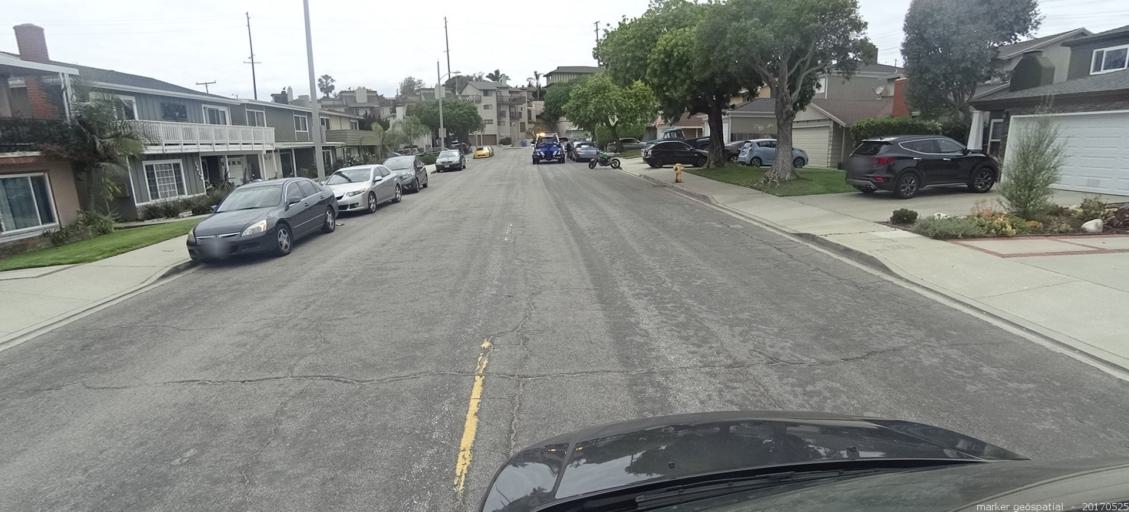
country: US
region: California
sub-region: Los Angeles County
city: Redondo Beach
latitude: 33.8553
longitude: -118.3816
